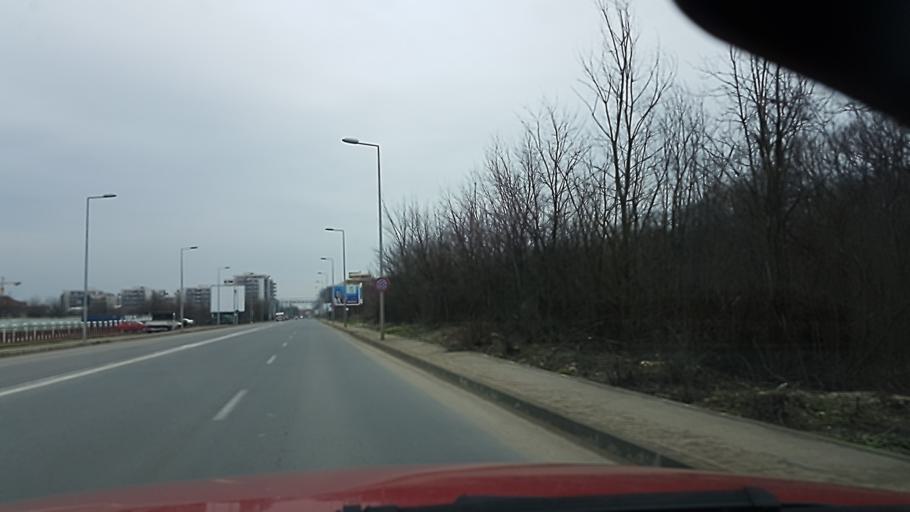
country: RO
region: Ilfov
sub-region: Comuna Tunari
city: Tunari
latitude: 44.5280
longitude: 26.1430
